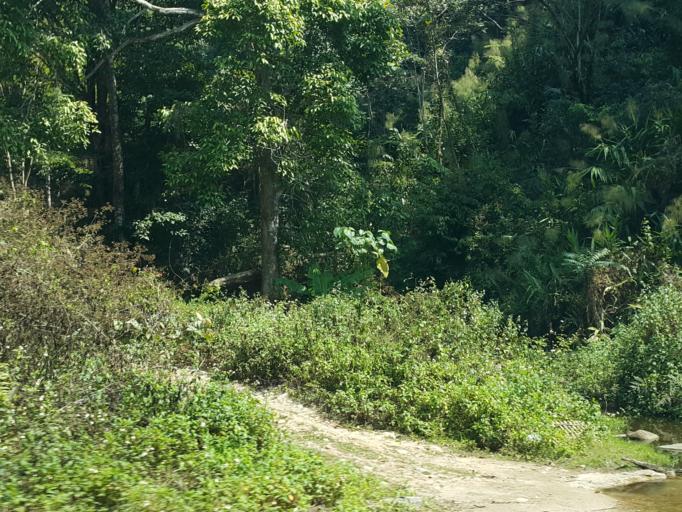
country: TH
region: Lampang
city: Mueang Pan
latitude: 18.8314
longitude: 99.3825
